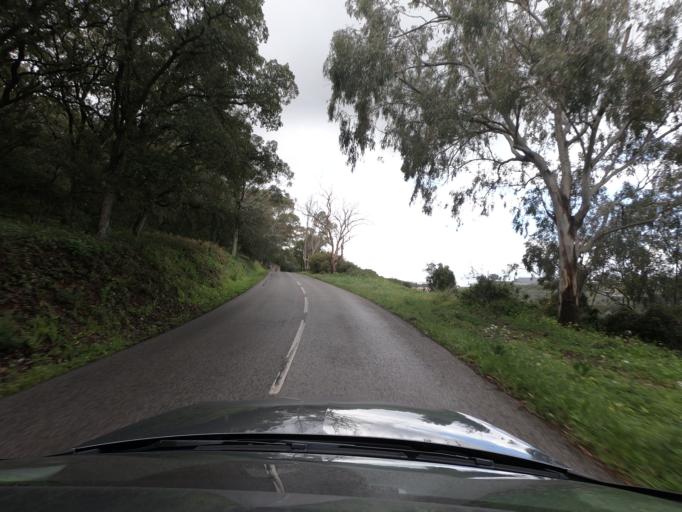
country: PT
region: Lisbon
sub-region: Sintra
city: Queluz
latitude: 38.7437
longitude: -9.2629
